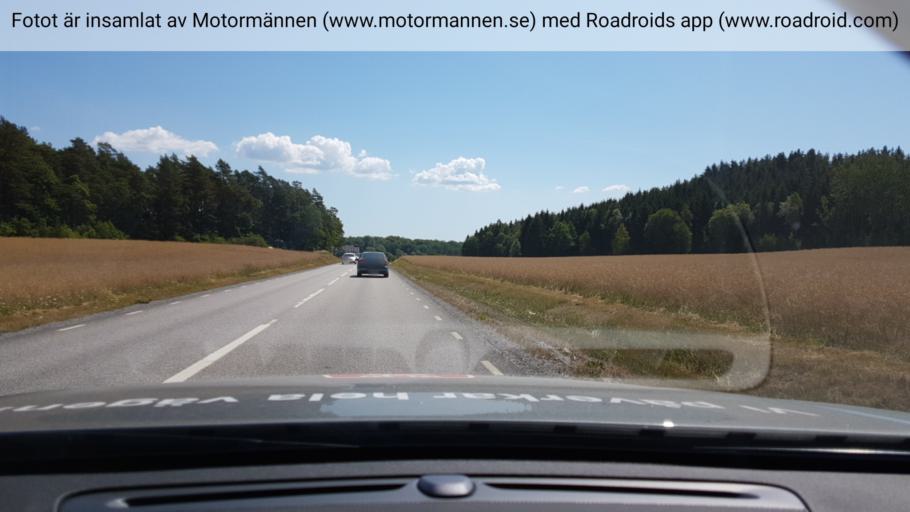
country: SE
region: Stockholm
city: Stenhamra
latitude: 59.3682
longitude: 17.7128
